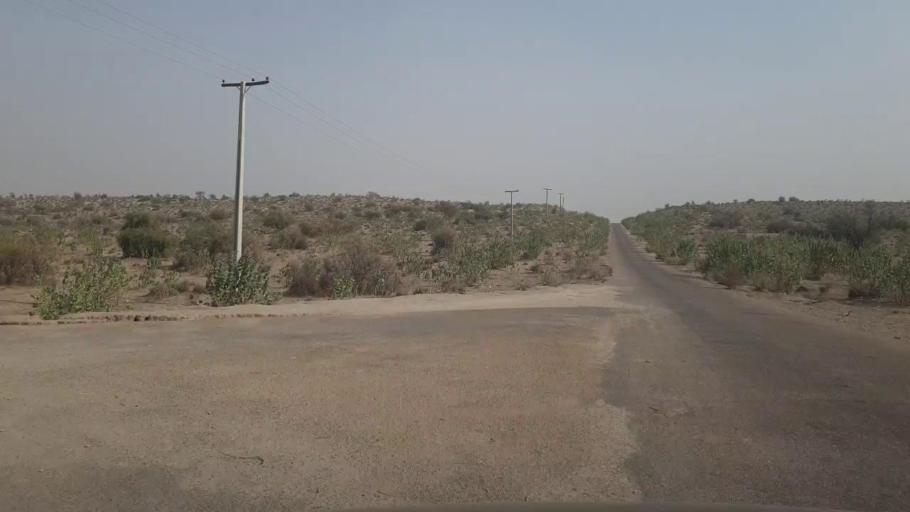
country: PK
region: Sindh
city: Chor
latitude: 25.6164
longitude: 69.9296
